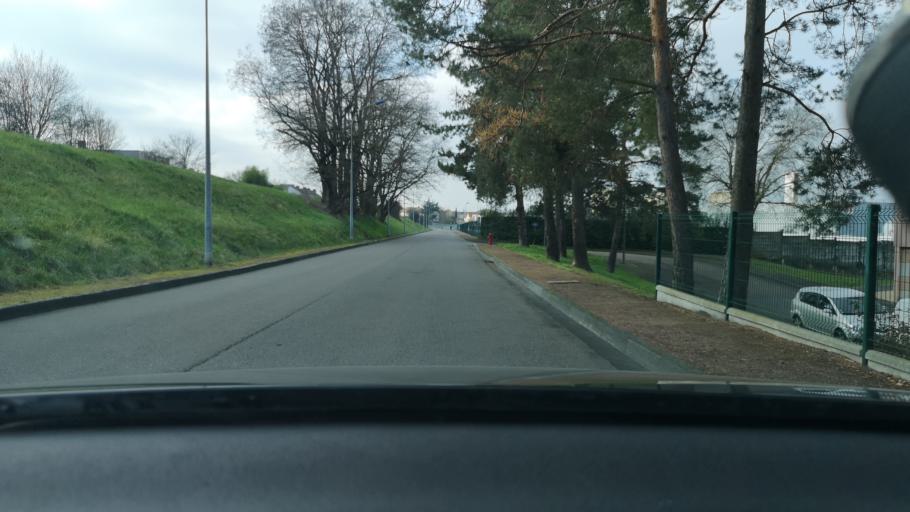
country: FR
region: Bourgogne
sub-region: Departement de Saone-et-Loire
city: Chalon-sur-Saone
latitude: 46.7935
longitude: 4.8373
